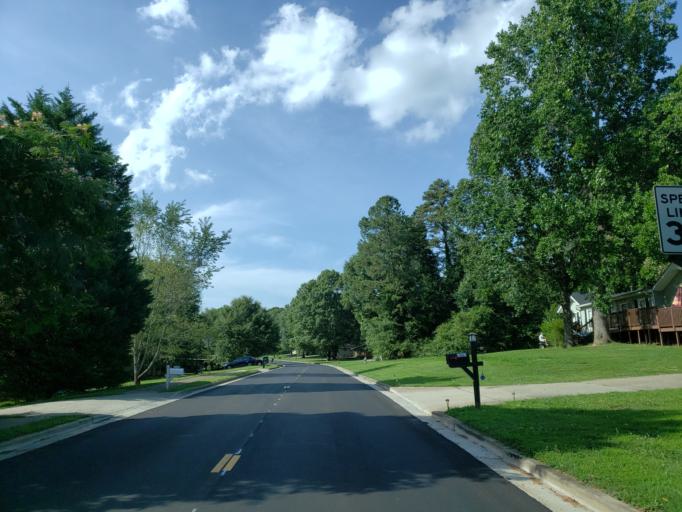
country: US
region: Georgia
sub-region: Cobb County
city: Powder Springs
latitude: 33.9071
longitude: -84.6863
